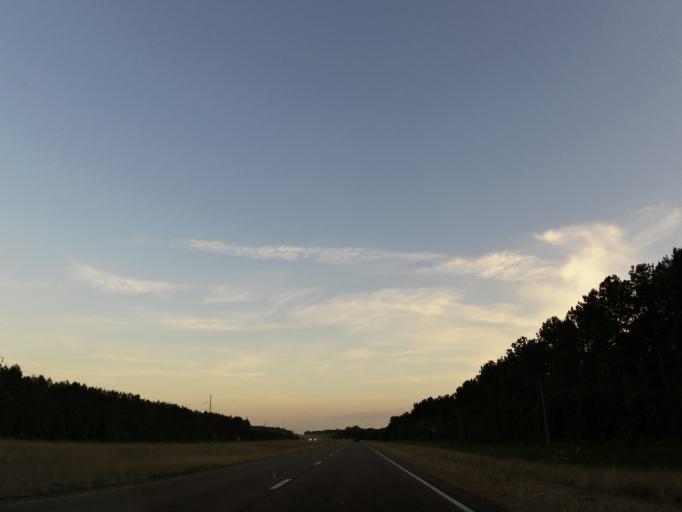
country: US
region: Mississippi
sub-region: Noxubee County
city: Macon
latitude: 33.0487
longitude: -88.5638
